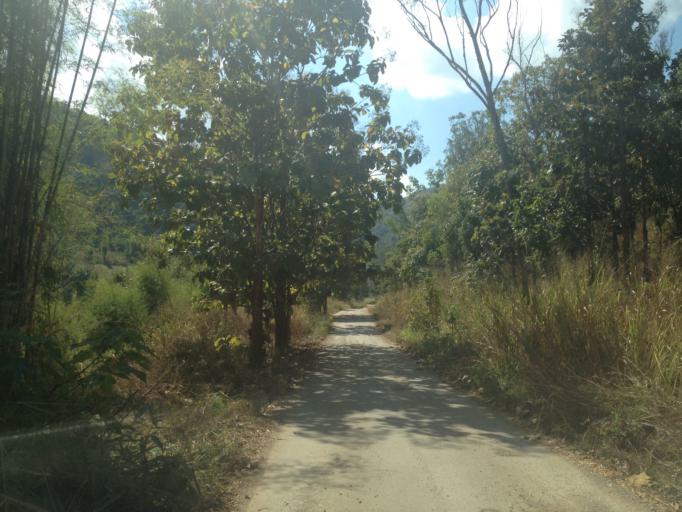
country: TH
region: Mae Hong Son
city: Ban Huai I Huak
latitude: 18.1040
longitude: 98.1910
